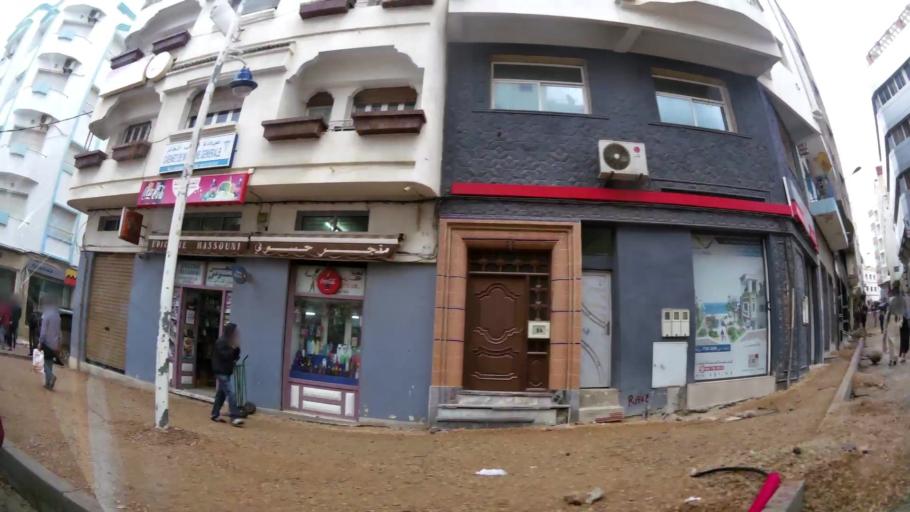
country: MA
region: Taza-Al Hoceima-Taounate
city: Al Hoceima
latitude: 35.2429
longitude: -3.9299
